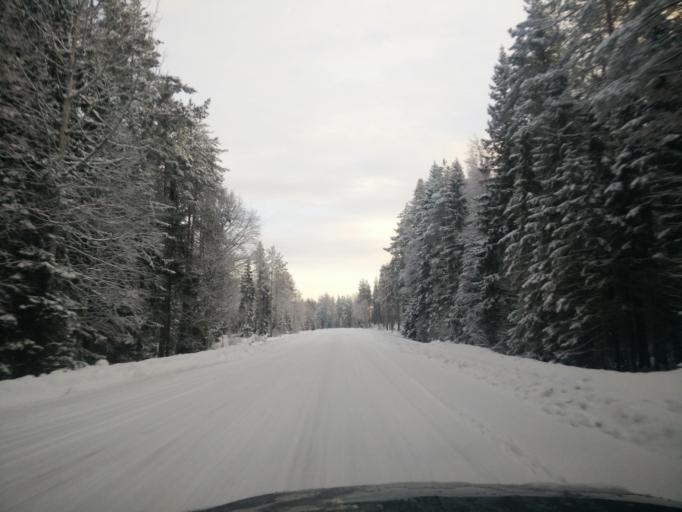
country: SE
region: Vaesternorrland
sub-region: Sundsvalls Kommun
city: Njurundabommen
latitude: 62.2153
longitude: 17.3680
